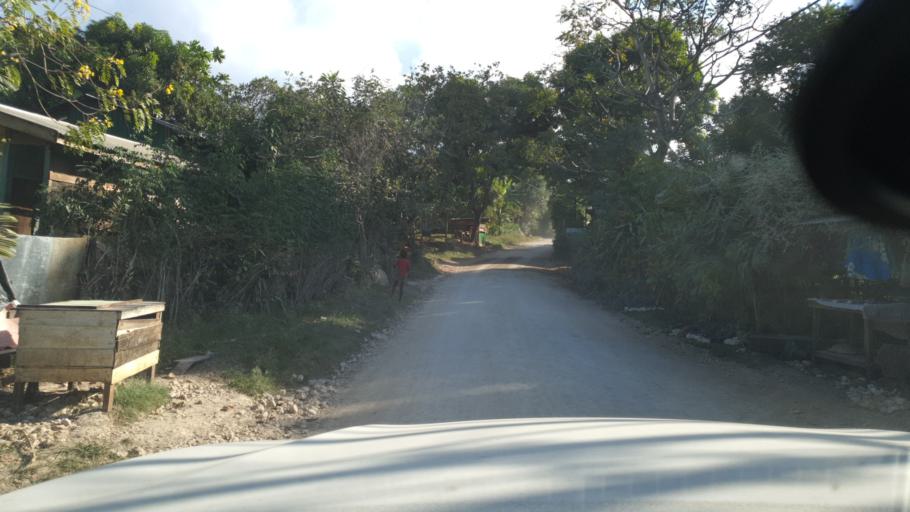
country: SB
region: Guadalcanal
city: Honiara
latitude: -9.4524
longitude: 159.9929
